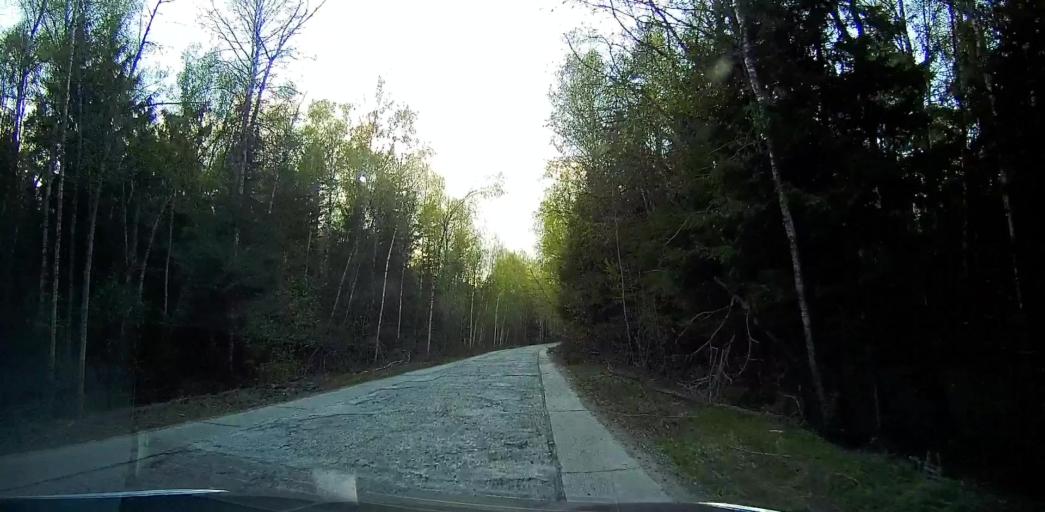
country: RU
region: Moskovskaya
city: Malyshevo
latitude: 55.5352
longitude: 38.3905
